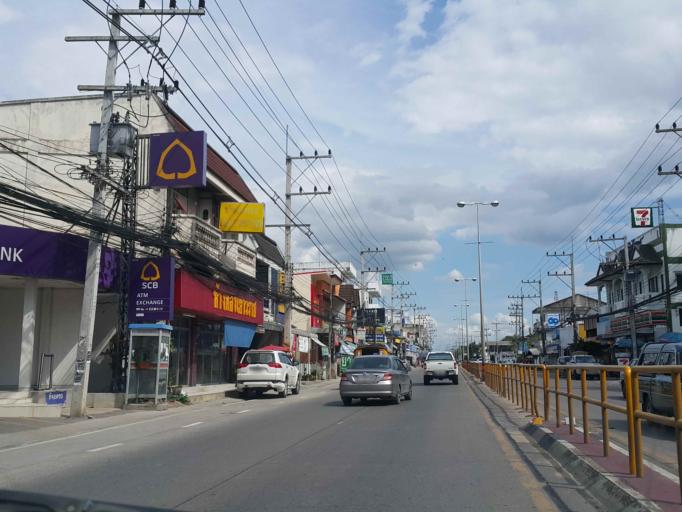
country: TH
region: Chiang Mai
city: San Sai
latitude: 18.9129
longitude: 98.9459
